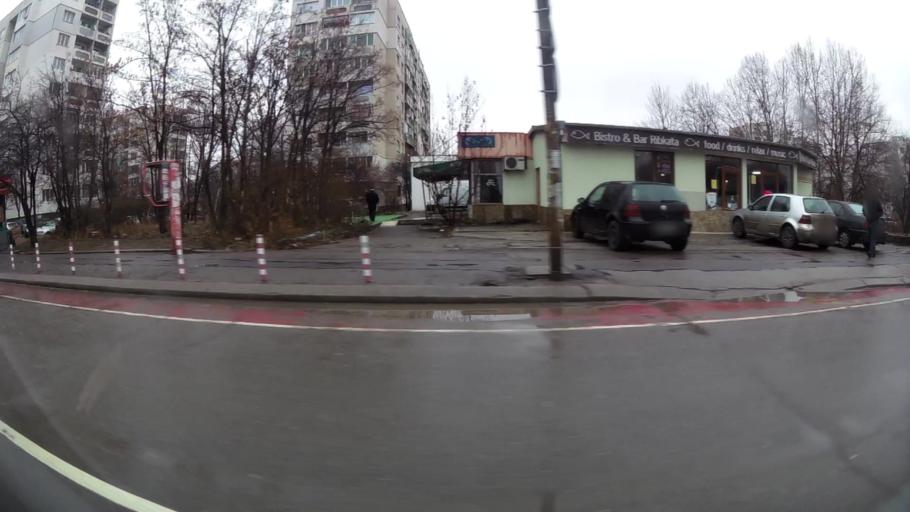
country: BG
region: Sofia-Capital
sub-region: Stolichna Obshtina
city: Sofia
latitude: 42.6307
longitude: 23.3751
